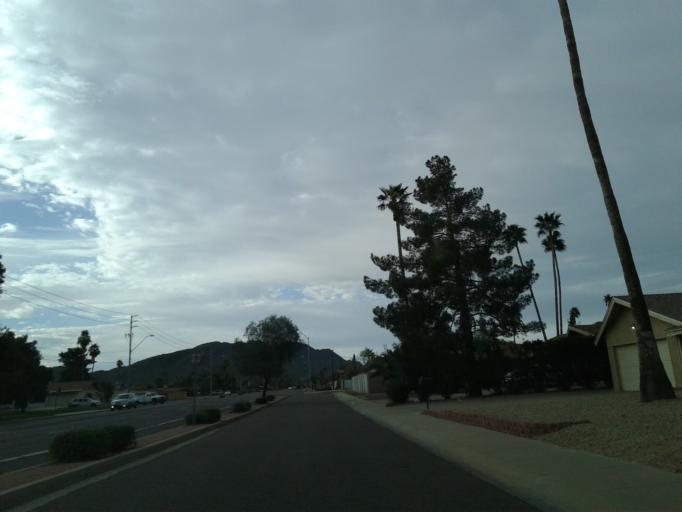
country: US
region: Arizona
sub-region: Maricopa County
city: Paradise Valley
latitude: 33.5887
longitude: -111.9959
